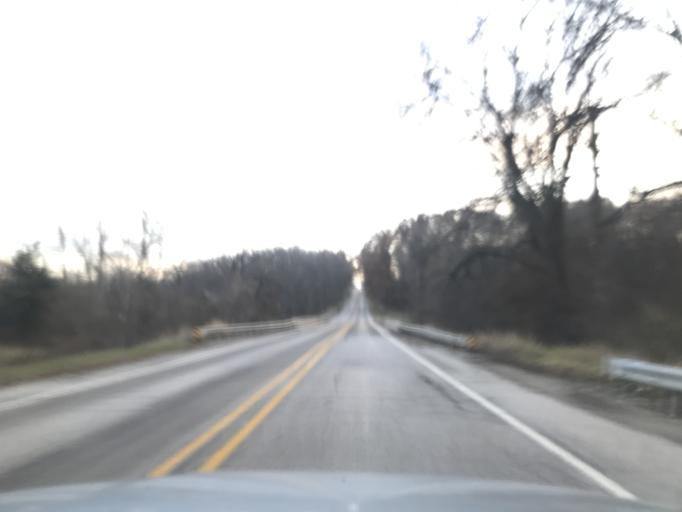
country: US
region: Illinois
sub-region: Henderson County
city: Oquawka
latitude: 40.9035
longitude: -90.8644
